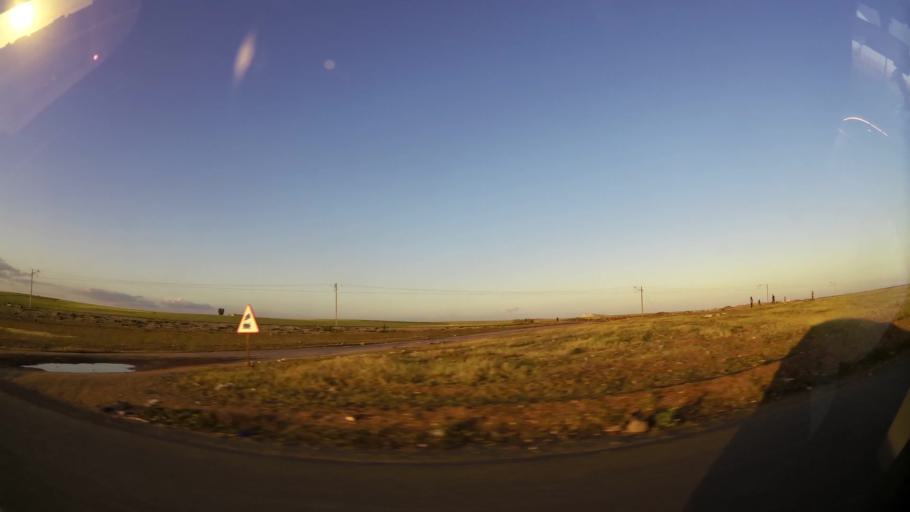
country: MA
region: Marrakech-Tensift-Al Haouz
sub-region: Kelaa-Des-Sraghna
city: Sidi Abdallah
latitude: 32.2386
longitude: -7.9286
